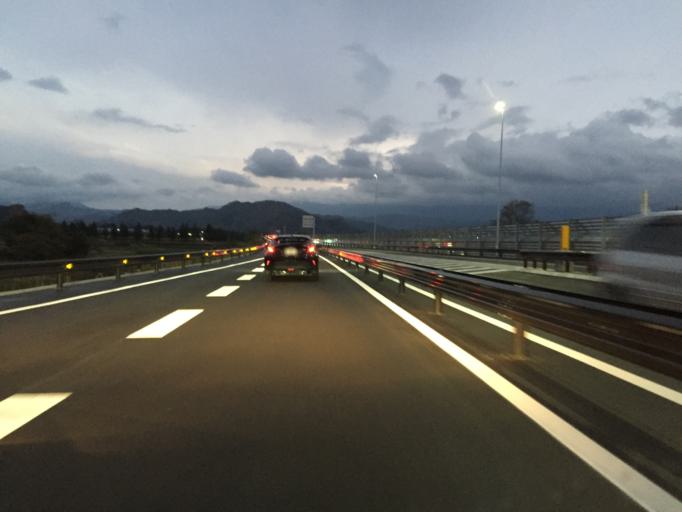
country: JP
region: Yamagata
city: Yonezawa
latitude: 37.9183
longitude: 140.1365
